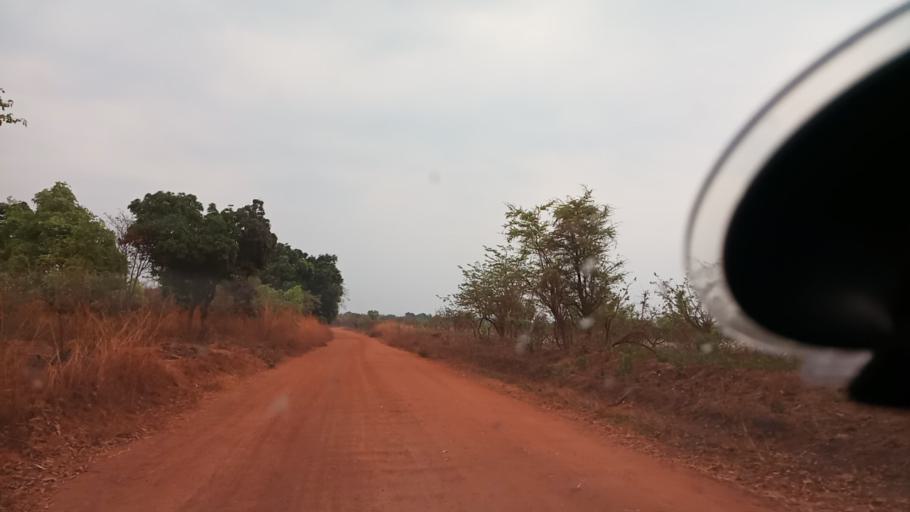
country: ZM
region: Luapula
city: Nchelenge
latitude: -9.1751
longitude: 28.2817
